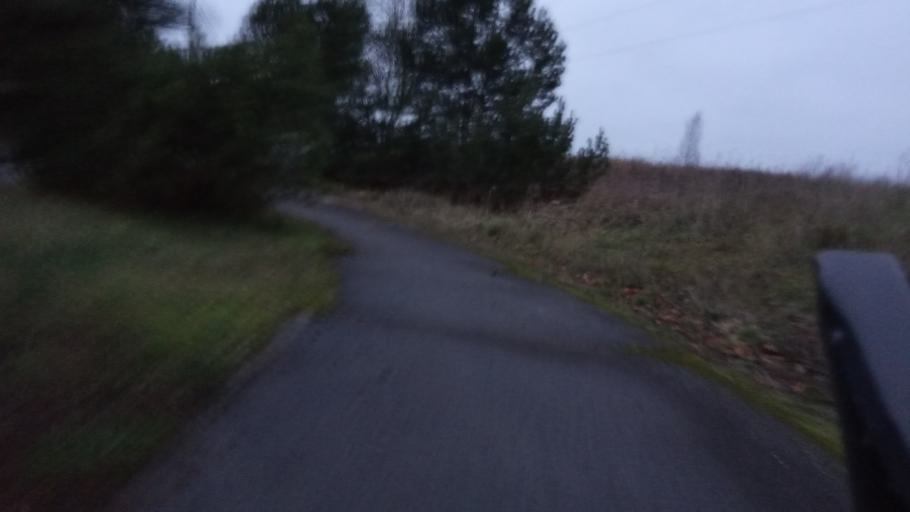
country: EE
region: Harju
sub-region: Kuusalu vald
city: Kuusalu
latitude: 59.4502
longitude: 25.4312
